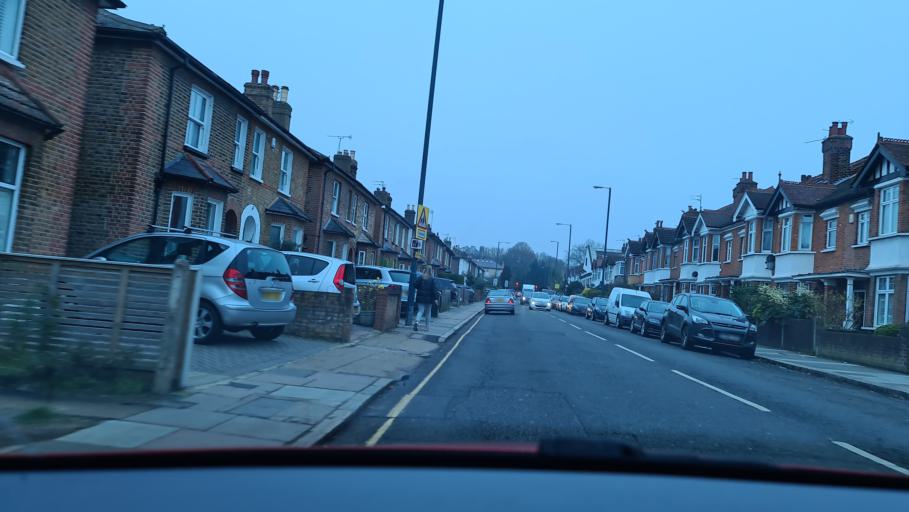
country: GB
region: England
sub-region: Greater London
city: Richmond
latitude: 51.4640
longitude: -0.2883
